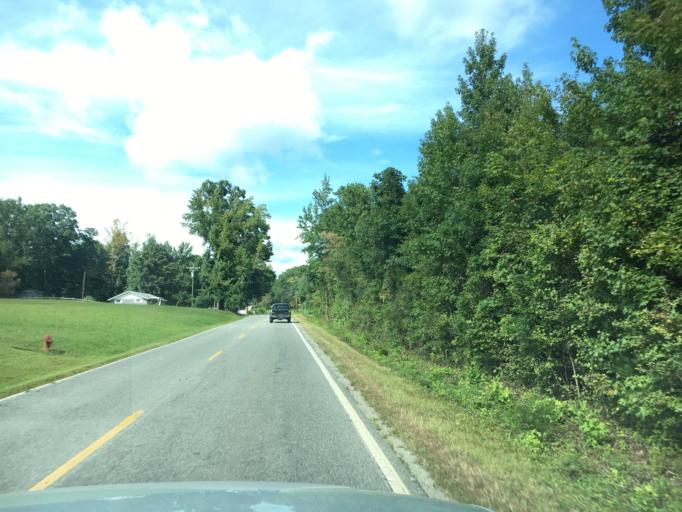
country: US
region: North Carolina
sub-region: Polk County
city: Columbus
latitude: 35.2797
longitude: -82.1797
